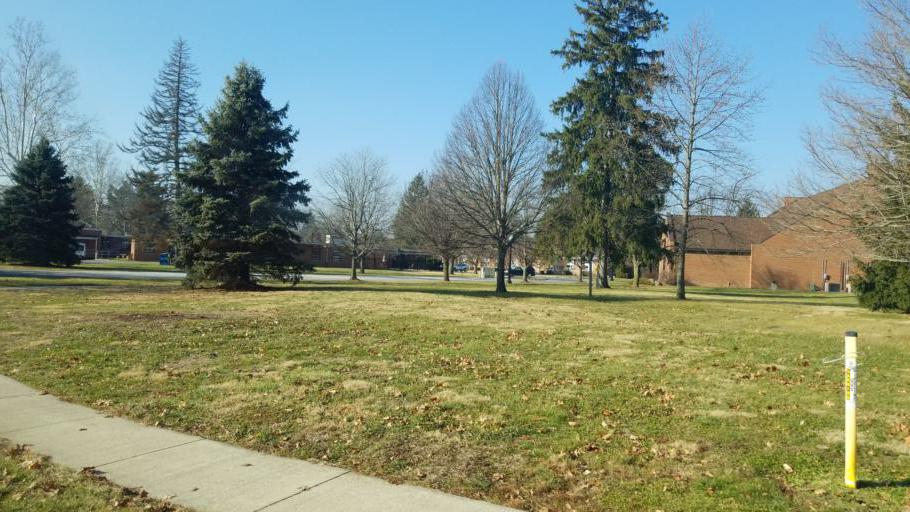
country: US
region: Ohio
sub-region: Seneca County
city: Tiffin
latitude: 41.1320
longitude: -83.1596
